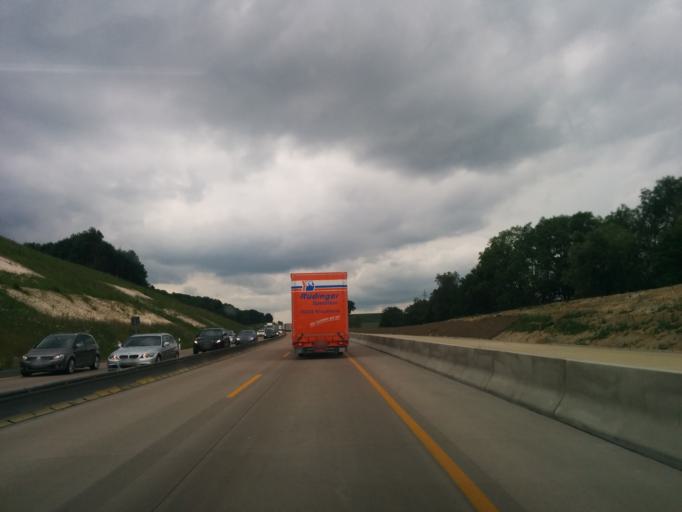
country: DE
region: Bavaria
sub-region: Swabia
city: Rettenbach
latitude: 48.4315
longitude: 10.3665
